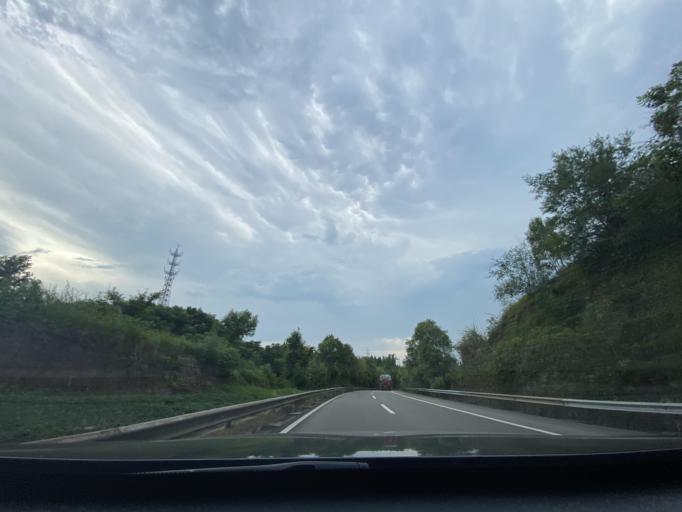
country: CN
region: Sichuan
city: Neijiang
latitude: 29.6803
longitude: 104.9564
